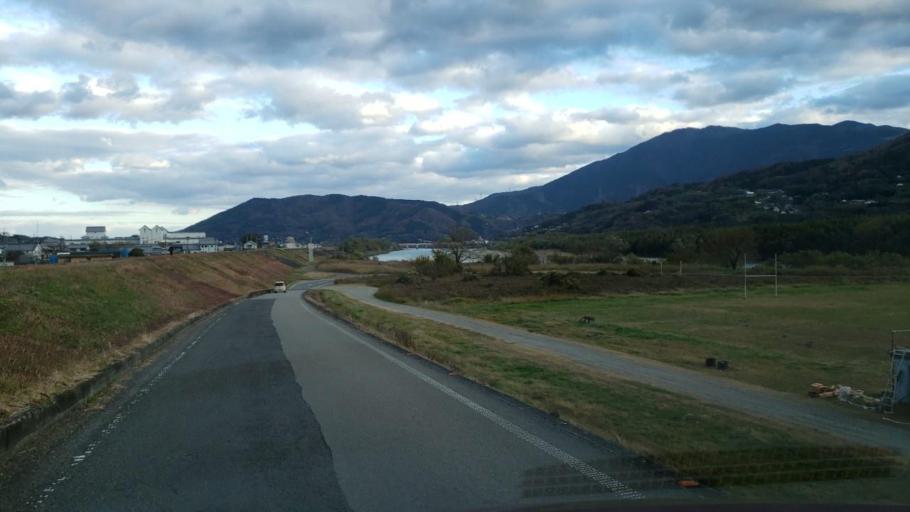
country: JP
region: Tokushima
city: Wakimachi
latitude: 34.0675
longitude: 134.1423
